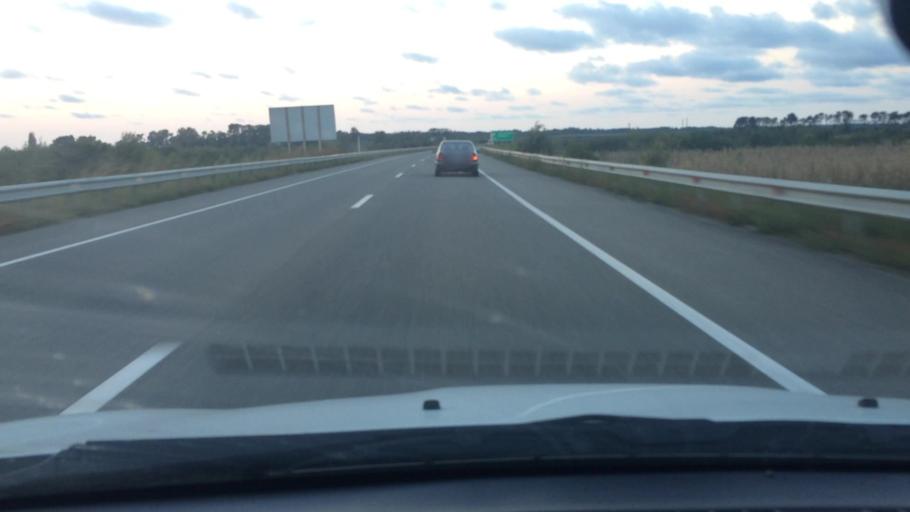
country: GE
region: Guria
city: Urek'i
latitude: 41.9102
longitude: 41.7828
